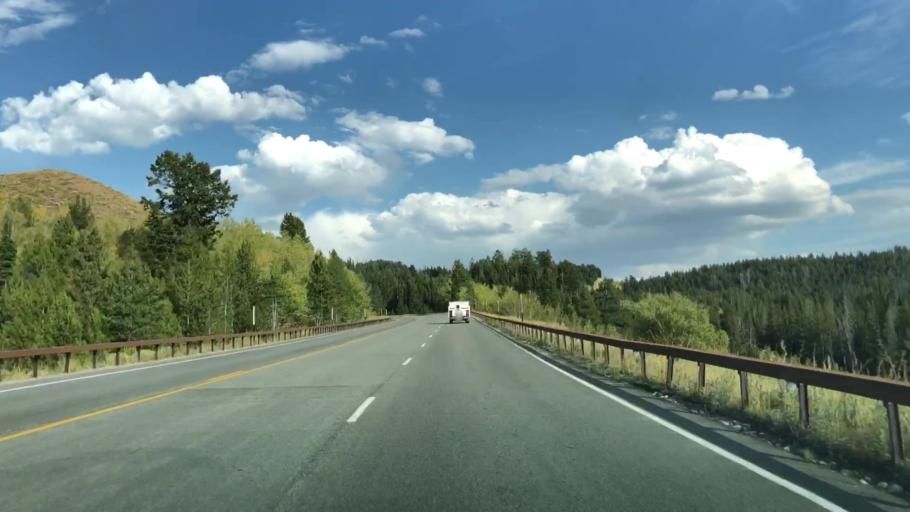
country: US
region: Wyoming
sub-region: Sublette County
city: Pinedale
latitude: 43.1390
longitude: -110.2170
